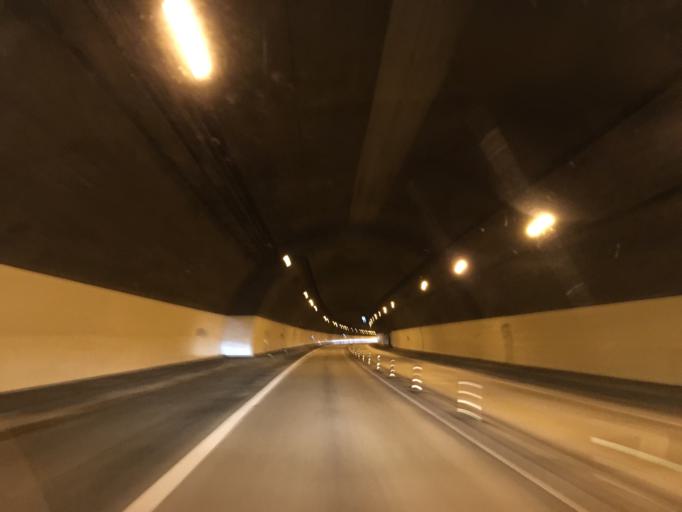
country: JP
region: Miyagi
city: Wakuya
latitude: 38.6317
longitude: 141.2801
